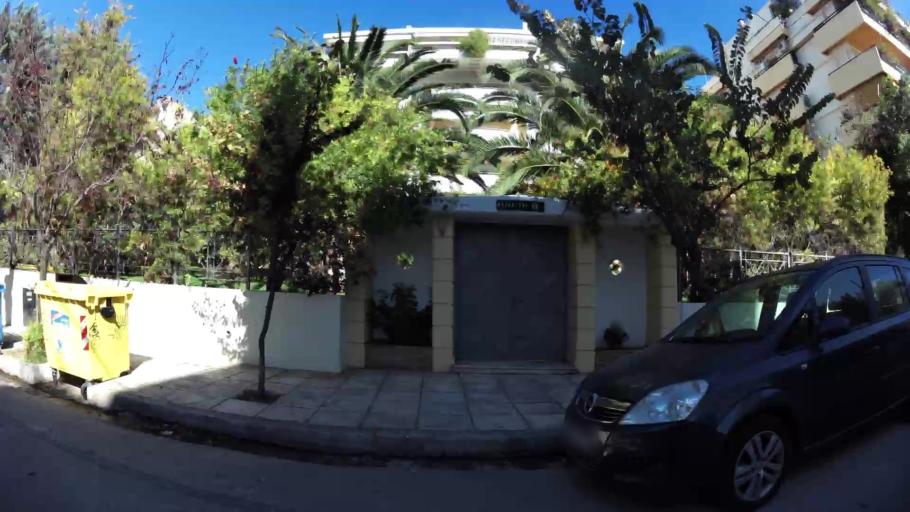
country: GR
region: Attica
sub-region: Nomarchia Athinas
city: Khalandrion
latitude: 38.0289
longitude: 23.8036
